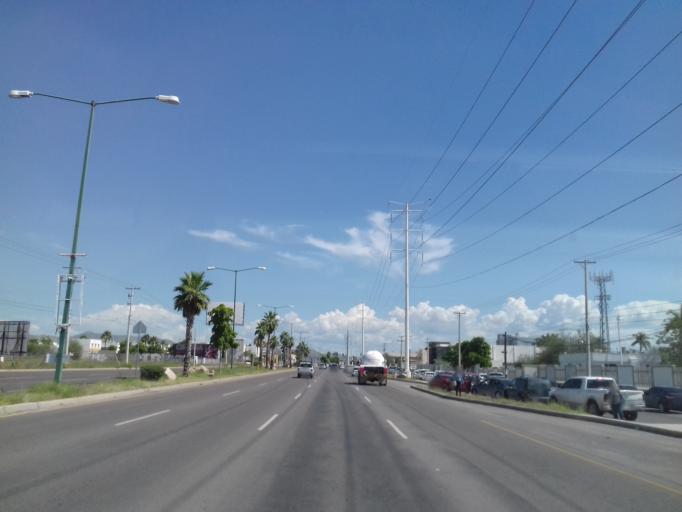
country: MX
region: Sonora
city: Hermosillo
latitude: 29.0837
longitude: -111.0002
